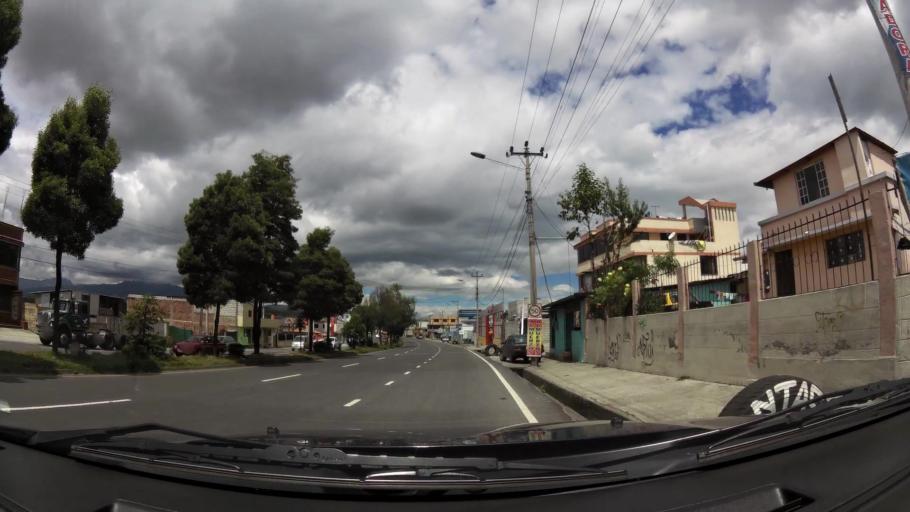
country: EC
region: Pichincha
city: Sangolqui
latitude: -0.3507
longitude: -78.5495
